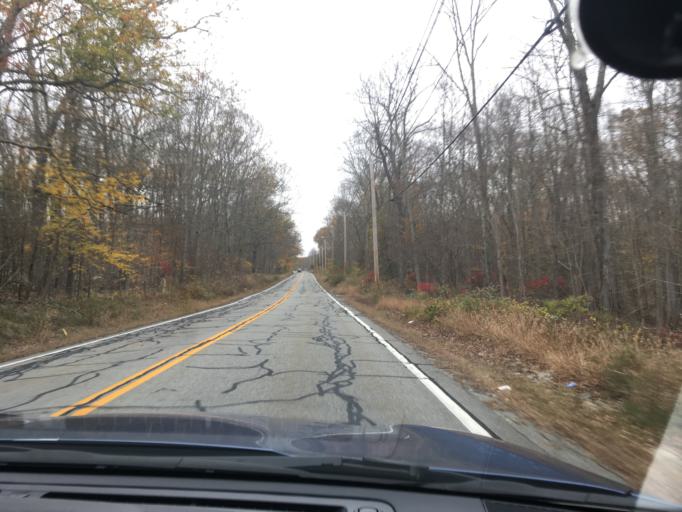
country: US
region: Rhode Island
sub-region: Providence County
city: North Scituate
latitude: 41.7971
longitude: -71.6581
